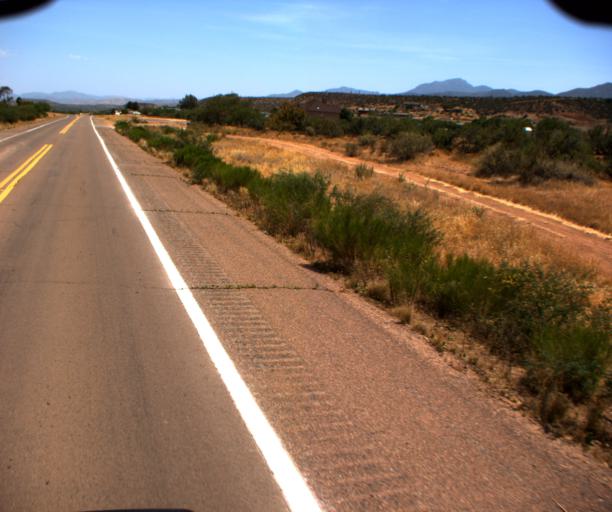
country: US
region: Arizona
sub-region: Gila County
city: Tonto Basin
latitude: 33.8485
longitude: -111.3094
